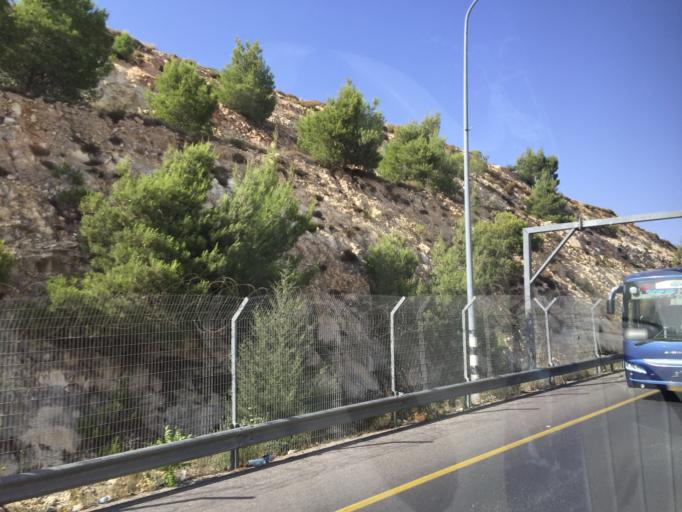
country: PS
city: Khallat Hamamah
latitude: 31.7258
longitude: 35.1917
